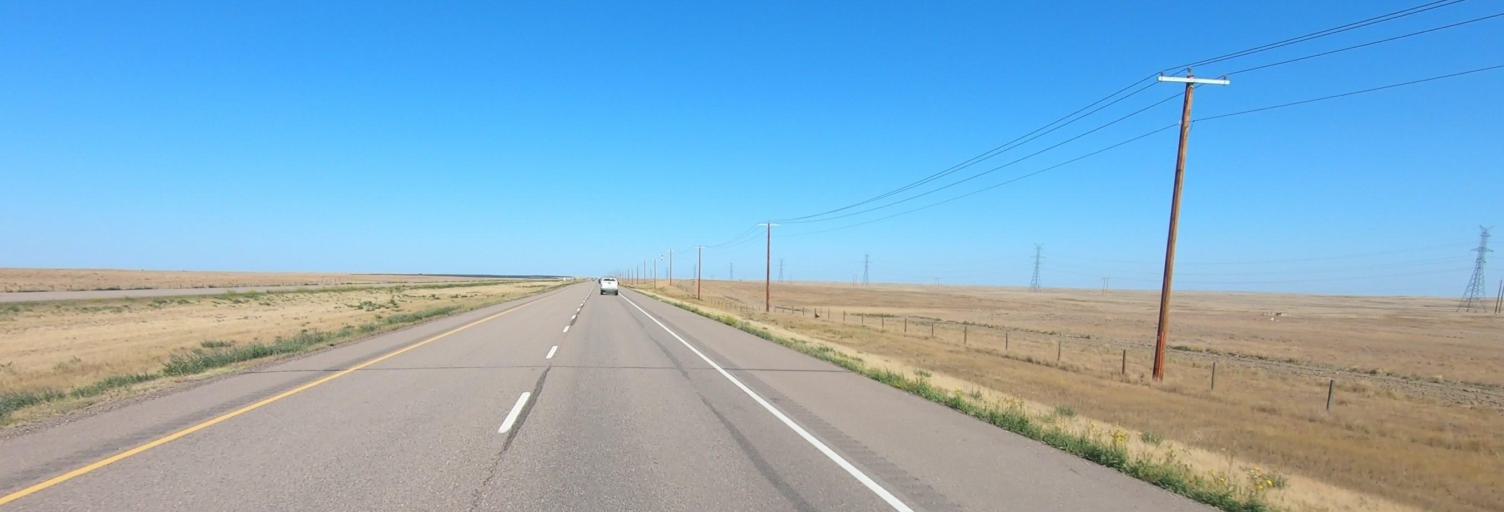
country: CA
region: Alberta
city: Bow Island
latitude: 50.2506
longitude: -111.2302
